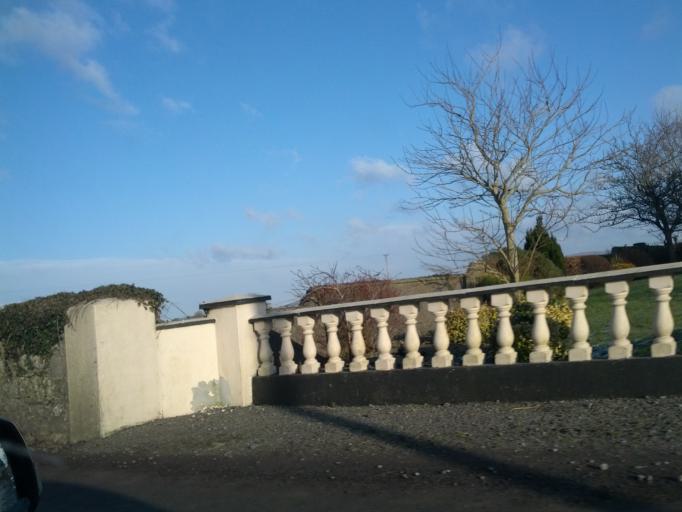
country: IE
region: Connaught
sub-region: County Galway
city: Gort
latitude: 53.1477
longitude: -8.7938
